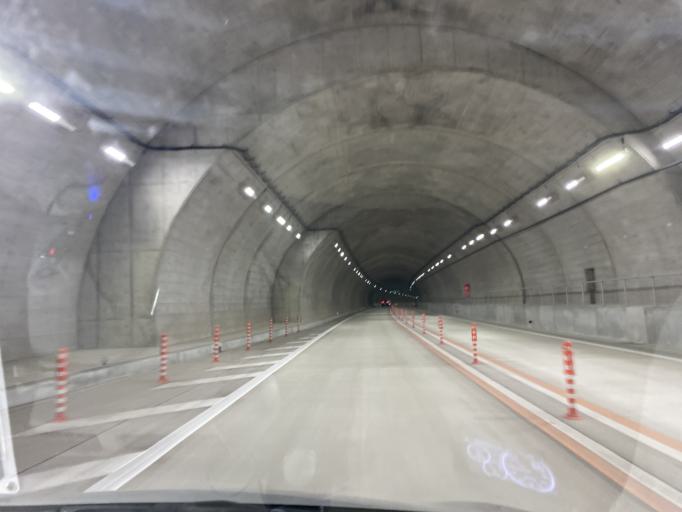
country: JP
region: Hyogo
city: Toyooka
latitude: 35.5056
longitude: 134.8005
